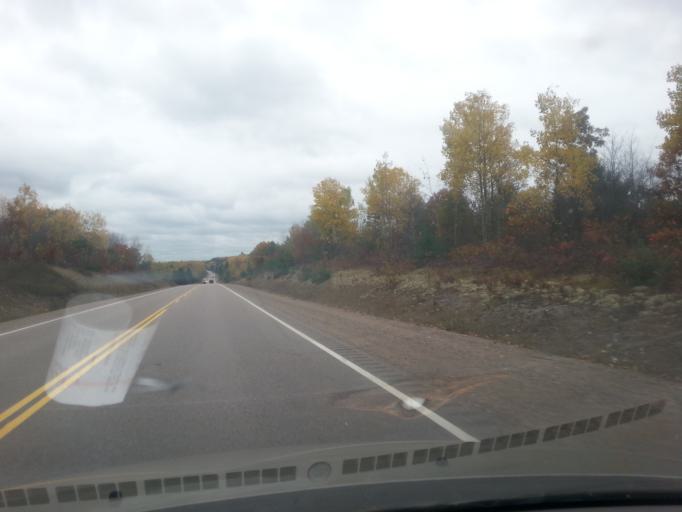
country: CA
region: Ontario
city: Mattawa
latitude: 46.2685
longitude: -78.3586
